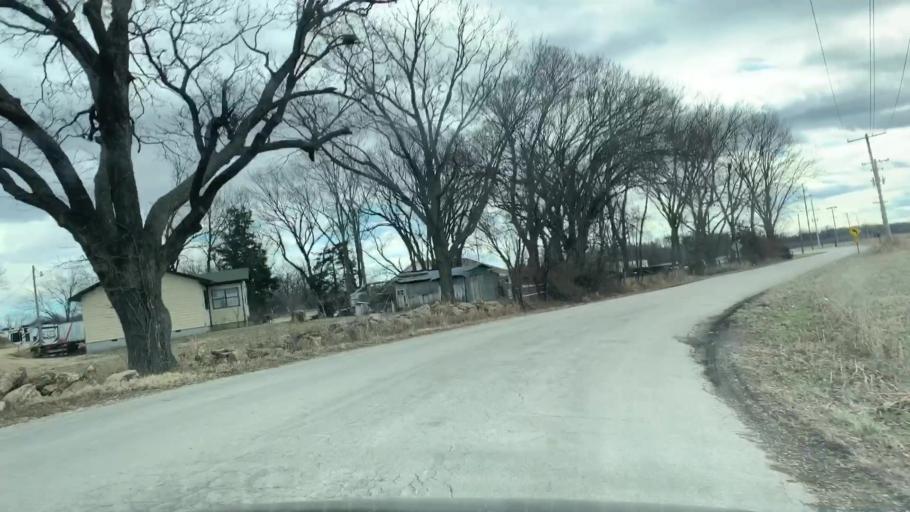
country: US
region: Kansas
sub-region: Allen County
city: Humboldt
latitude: 37.8126
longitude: -95.4525
